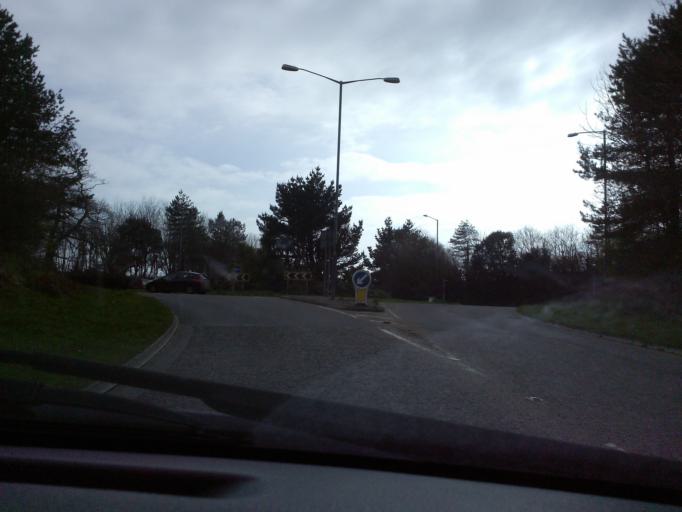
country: GB
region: England
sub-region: Cornwall
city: Penzance
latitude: 50.1146
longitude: -5.5570
